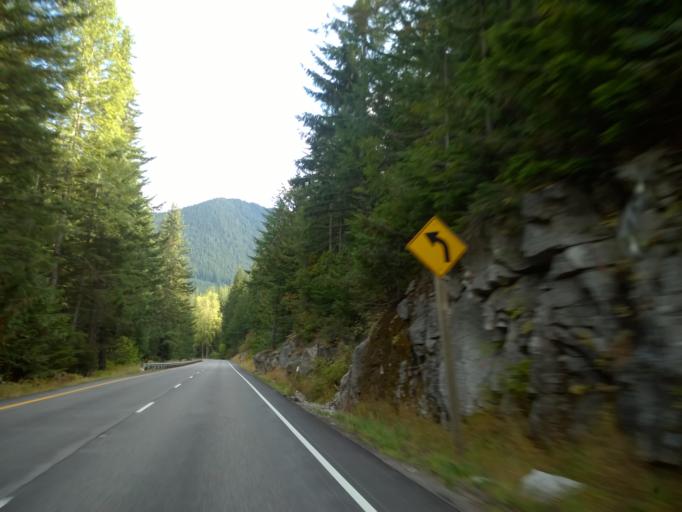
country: US
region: Washington
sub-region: Chelan County
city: Leavenworth
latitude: 47.7788
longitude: -121.0243
